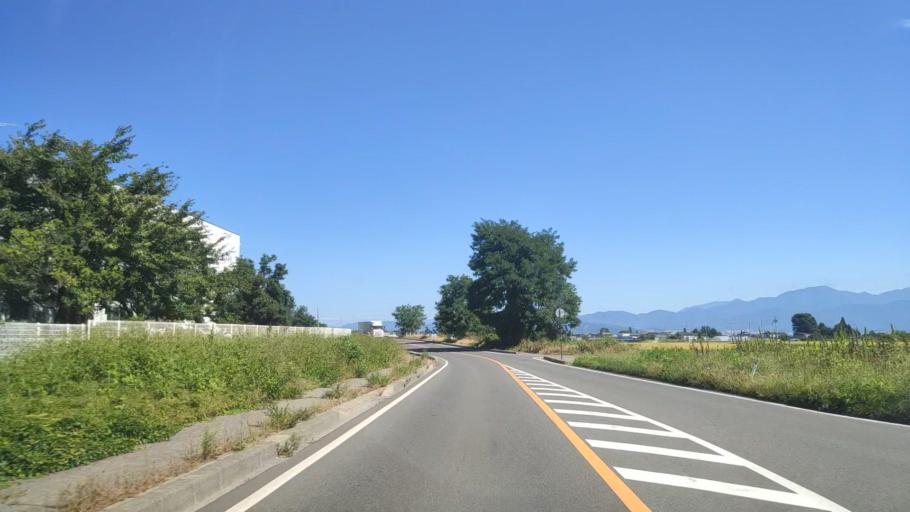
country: JP
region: Nagano
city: Matsumoto
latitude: 36.1831
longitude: 137.9046
